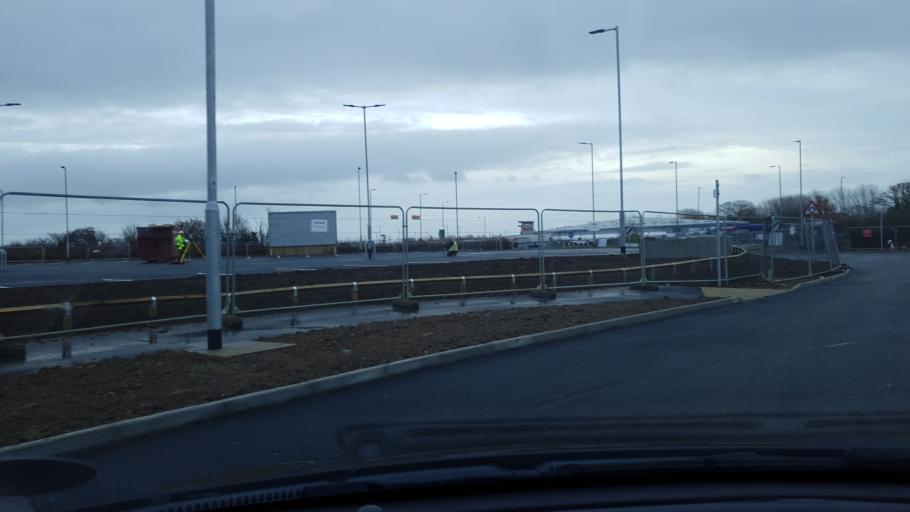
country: GB
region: England
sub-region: Essex
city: Little Clacton
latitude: 51.8111
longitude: 1.1437
